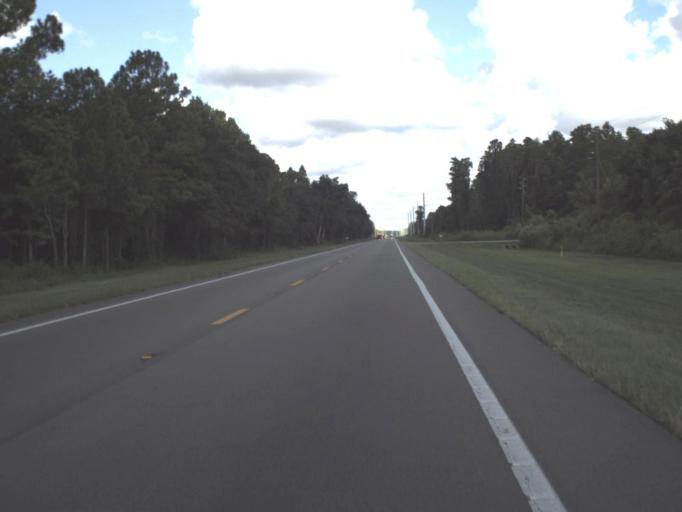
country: US
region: Florida
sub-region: Polk County
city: Kathleen
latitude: 28.2230
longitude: -82.0271
